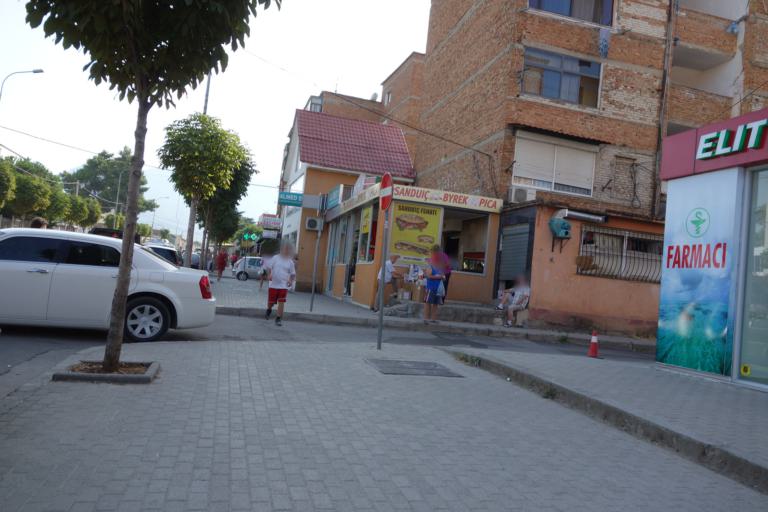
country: AL
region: Tirane
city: Tirana
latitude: 41.3387
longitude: 19.8351
